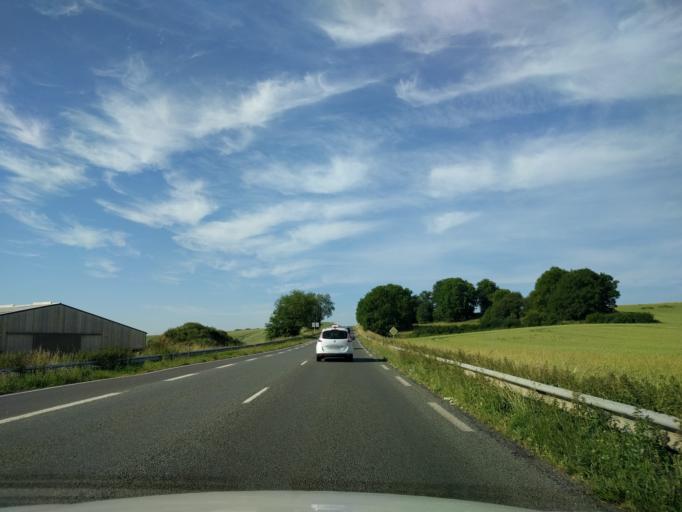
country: FR
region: Picardie
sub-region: Departement de l'Oise
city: Tille
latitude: 49.5346
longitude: 2.1969
